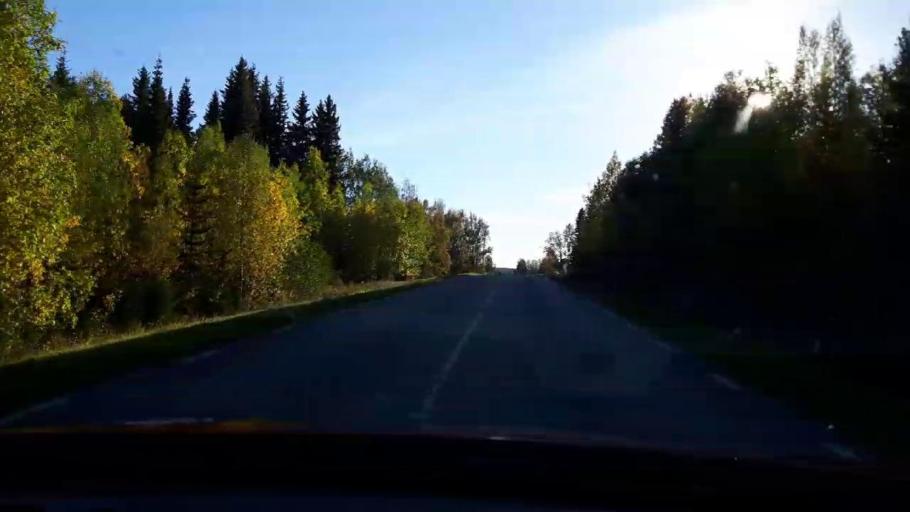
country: SE
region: Jaemtland
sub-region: OEstersunds Kommun
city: Lit
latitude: 63.8177
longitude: 14.8137
